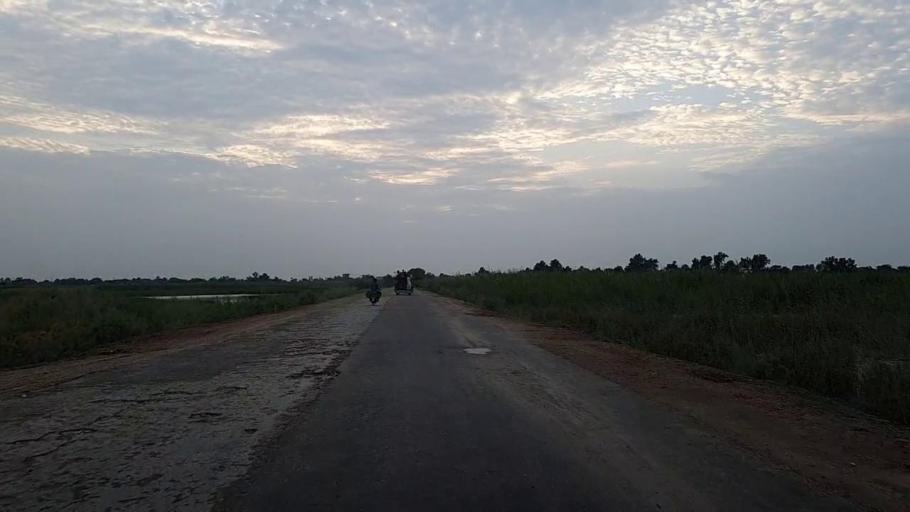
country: PK
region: Sindh
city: Naushahro Firoz
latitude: 26.8163
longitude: 68.1807
